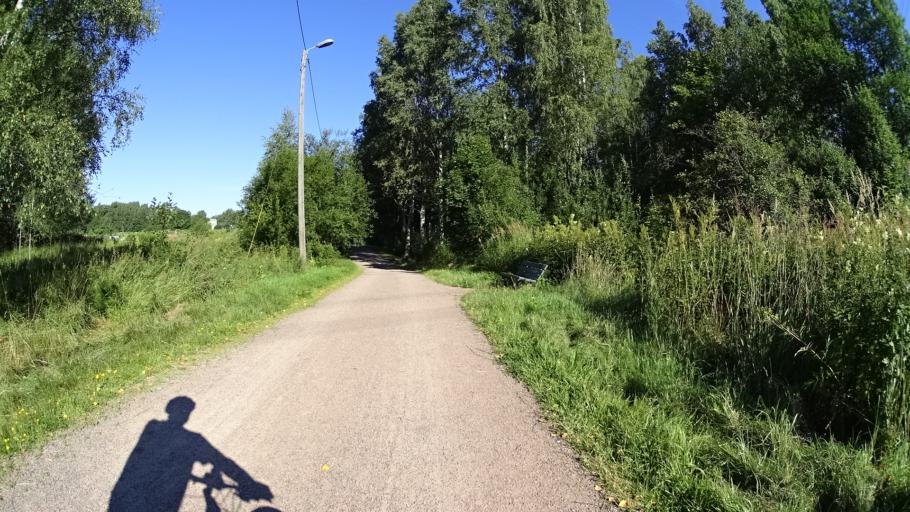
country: FI
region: Uusimaa
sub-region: Helsinki
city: Teekkarikylae
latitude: 60.2514
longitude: 24.8756
